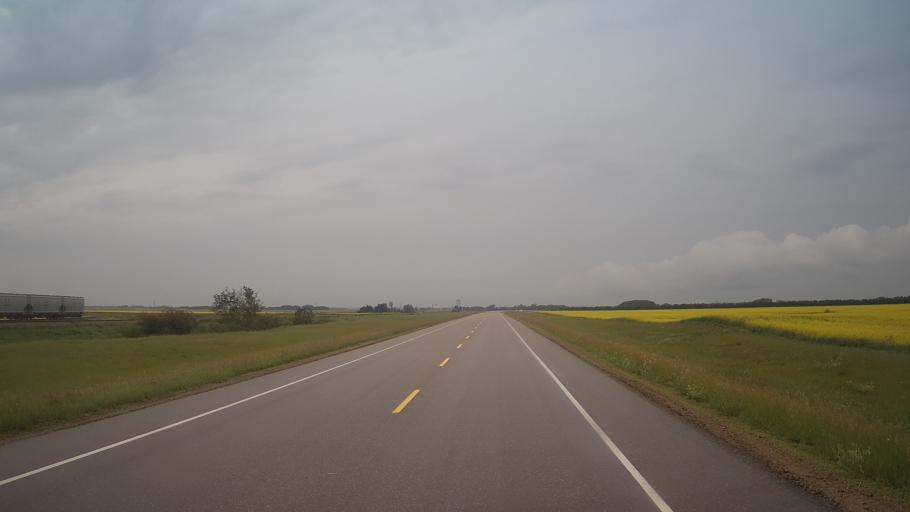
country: CA
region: Saskatchewan
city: Wilkie
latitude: 52.3064
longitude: -108.6838
